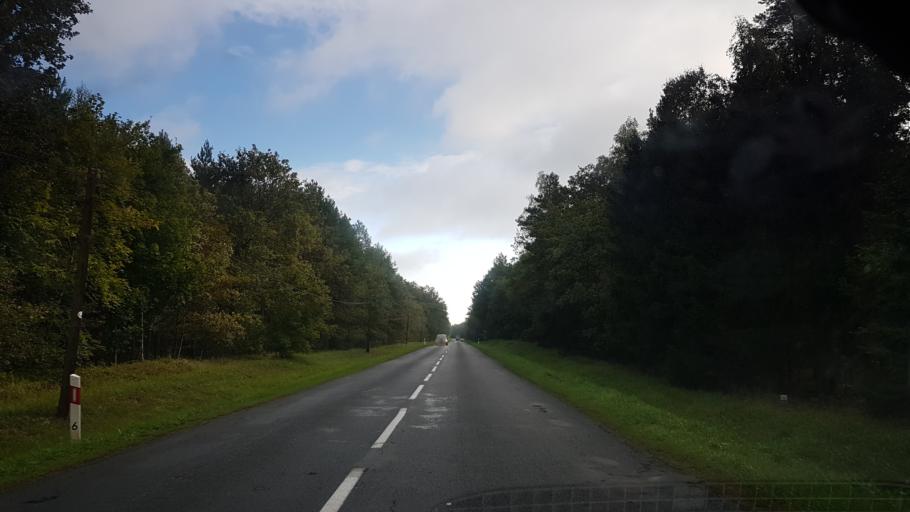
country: PL
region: Greater Poland Voivodeship
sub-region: Leszno
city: Leszno
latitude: 51.7961
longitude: 16.5696
